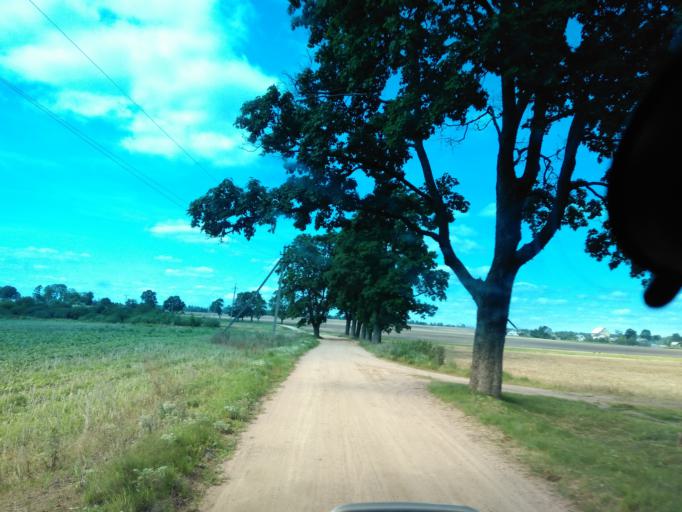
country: BY
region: Minsk
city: Stan'kava
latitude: 53.6330
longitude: 27.3122
